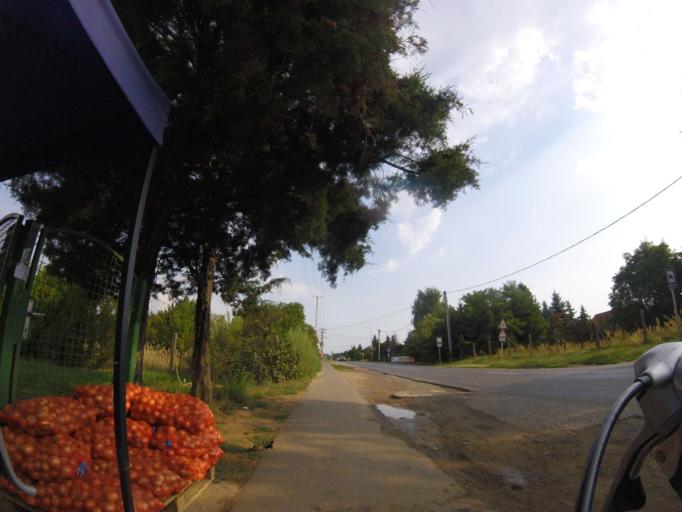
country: HU
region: Szabolcs-Szatmar-Bereg
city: Kotaj
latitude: 48.0347
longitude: 21.7479
